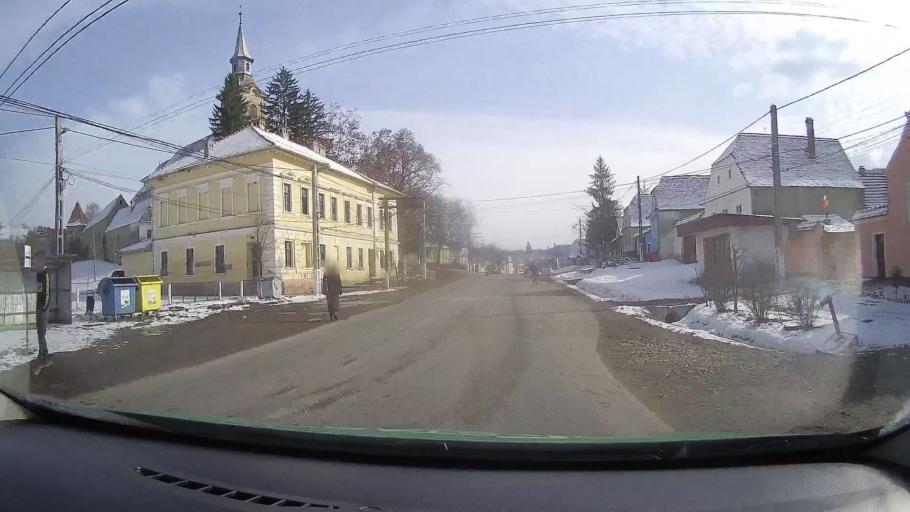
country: RO
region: Mures
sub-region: Comuna Apold
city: Saes
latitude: 46.1560
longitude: 24.7687
